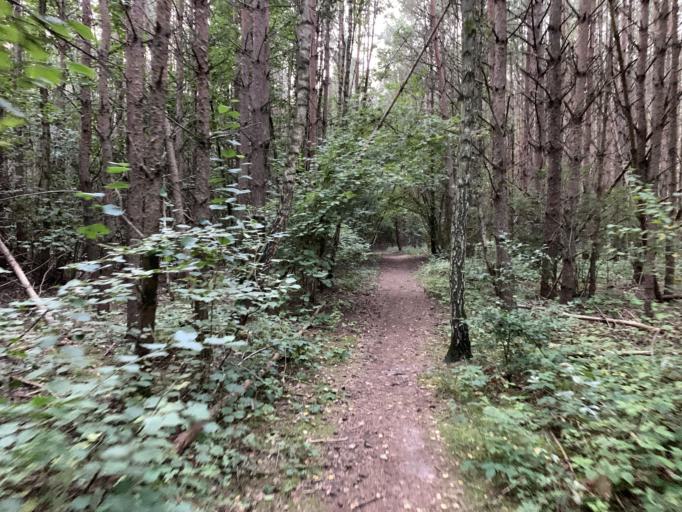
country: DE
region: Mecklenburg-Vorpommern
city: Blankensee
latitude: 53.4014
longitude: 13.2609
